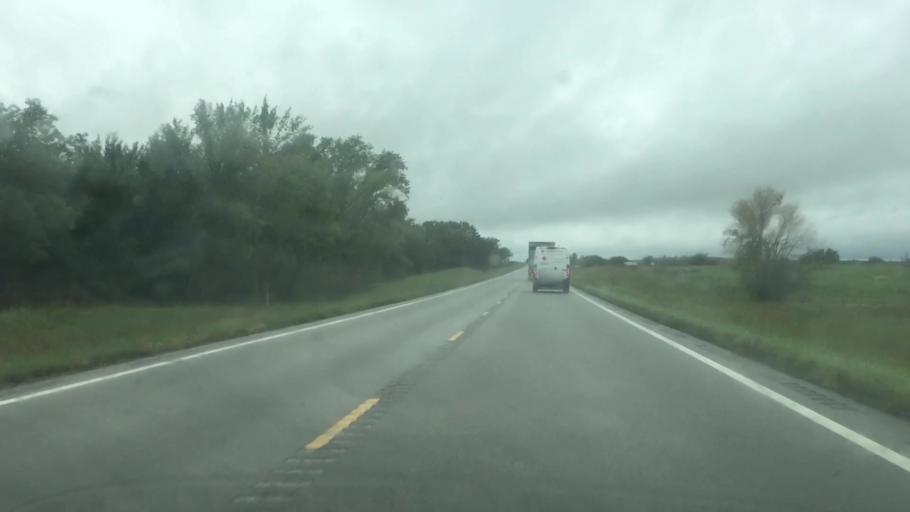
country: US
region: Kansas
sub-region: Allen County
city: Iola
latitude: 38.1011
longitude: -95.3561
